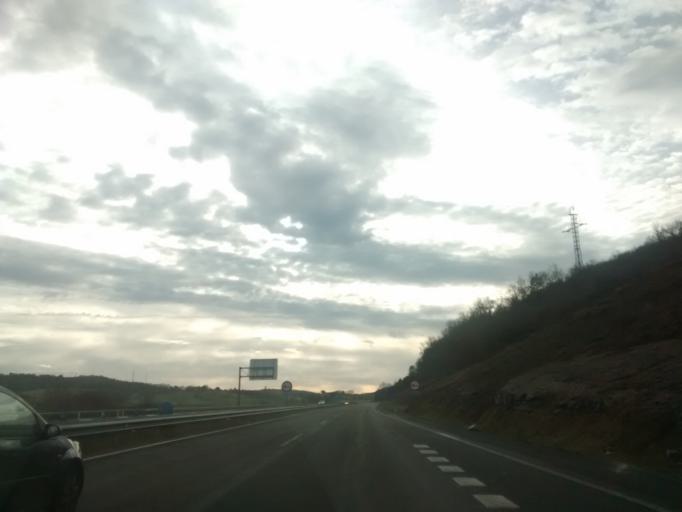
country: ES
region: Basque Country
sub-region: Provincia de Alava
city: Murguia
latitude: 42.9544
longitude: -2.8014
